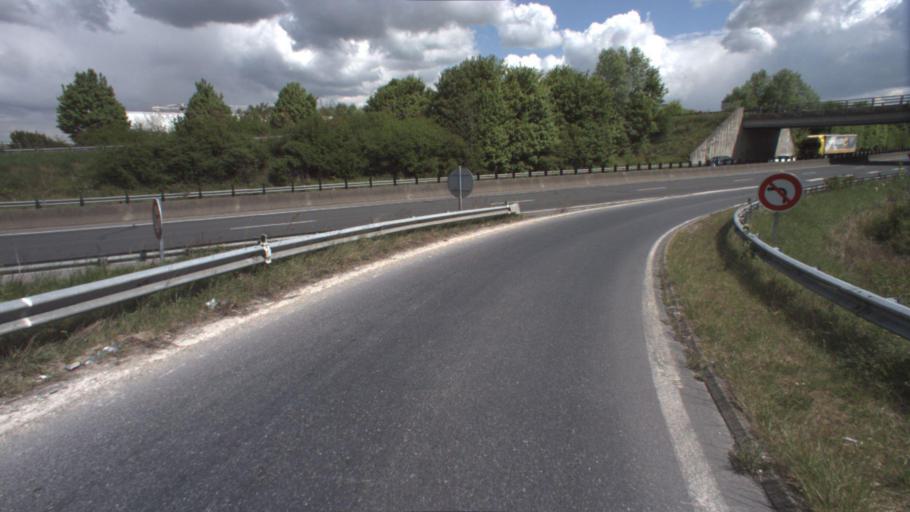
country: FR
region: Ile-de-France
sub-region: Departement de Seine-et-Marne
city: Tournan-en-Brie
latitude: 48.7341
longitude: 2.7769
